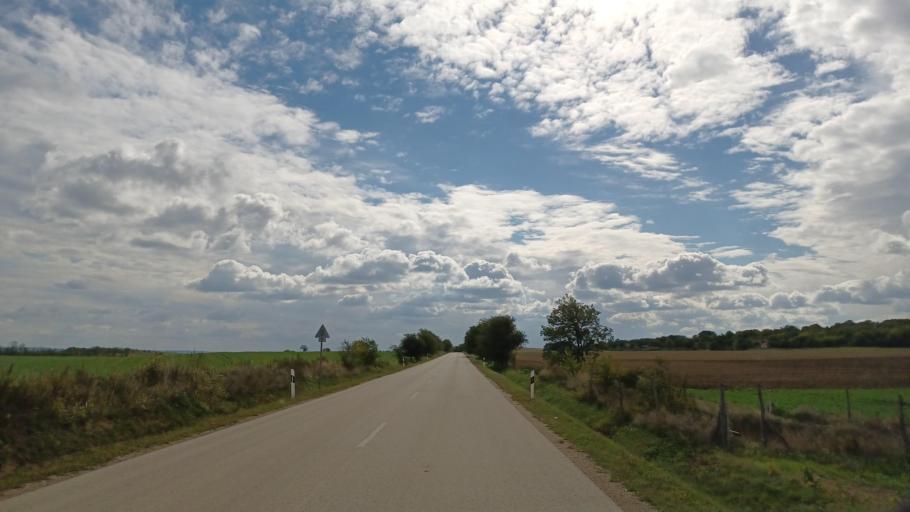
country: HU
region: Tolna
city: Simontornya
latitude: 46.7152
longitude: 18.5794
